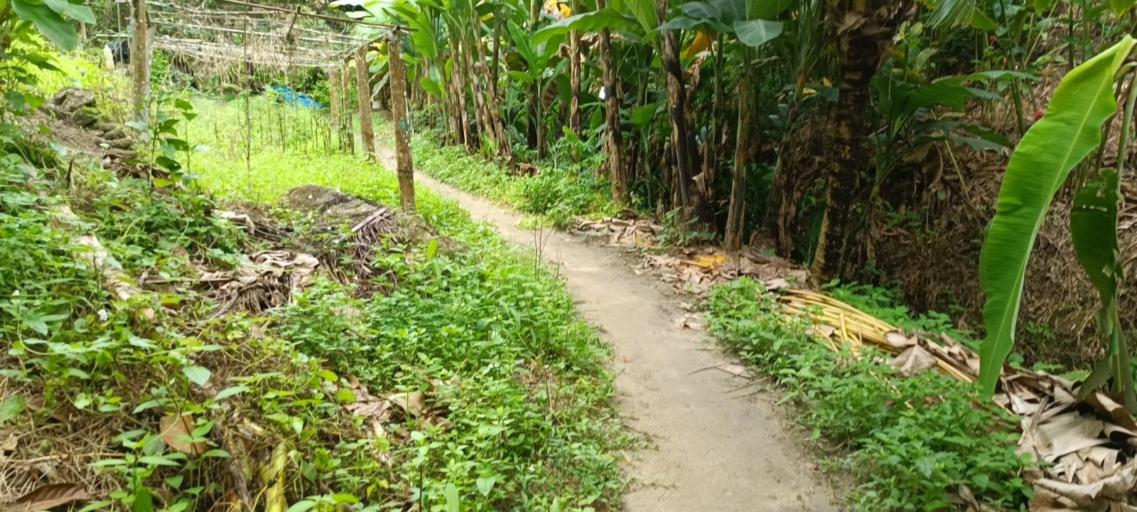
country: MY
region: Penang
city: George Town
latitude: 5.3839
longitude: 100.2897
